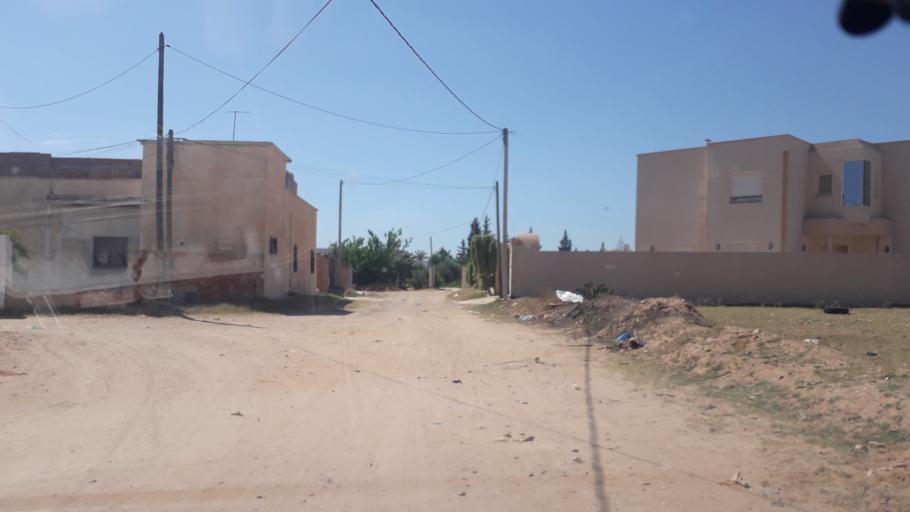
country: TN
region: Safaqis
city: Al Qarmadah
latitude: 34.8271
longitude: 10.7672
